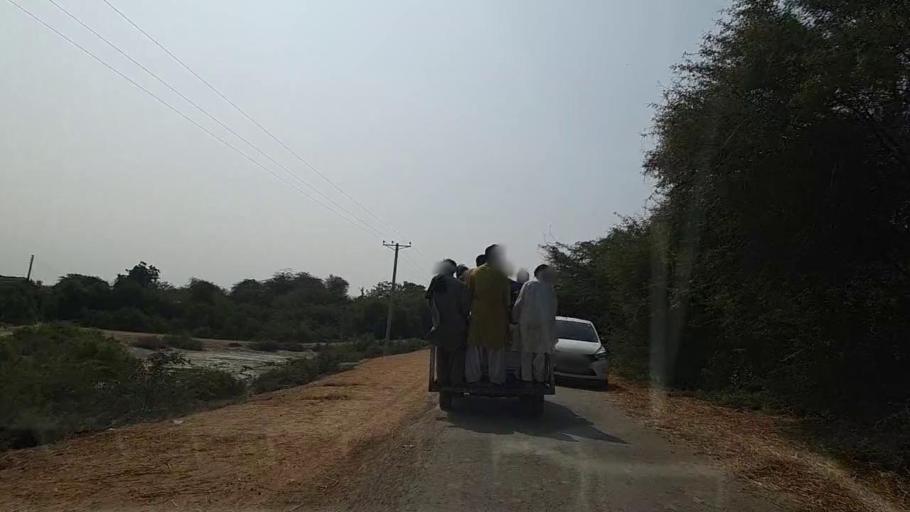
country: PK
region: Sindh
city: Chuhar Jamali
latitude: 24.3685
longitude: 67.9653
